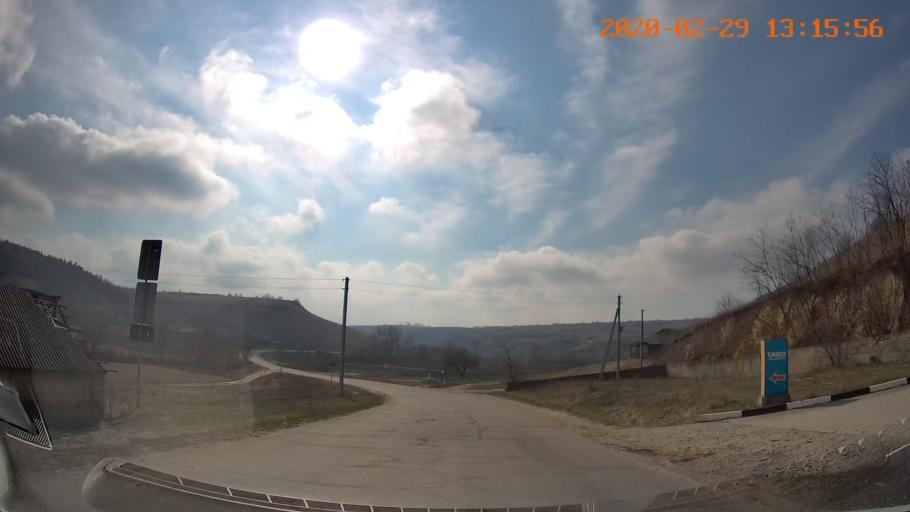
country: MD
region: Telenesti
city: Camenca
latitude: 48.0065
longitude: 28.6670
